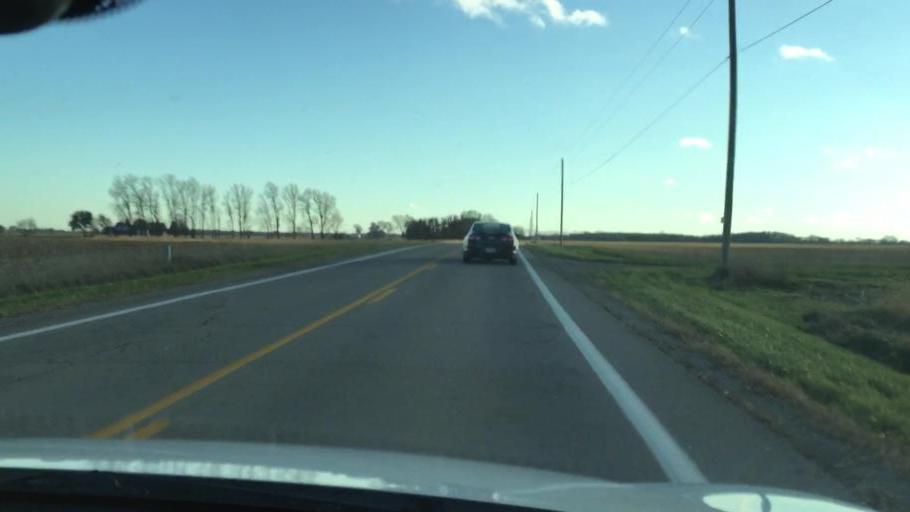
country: US
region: Ohio
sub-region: Champaign County
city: North Lewisburg
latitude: 40.1562
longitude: -83.5278
